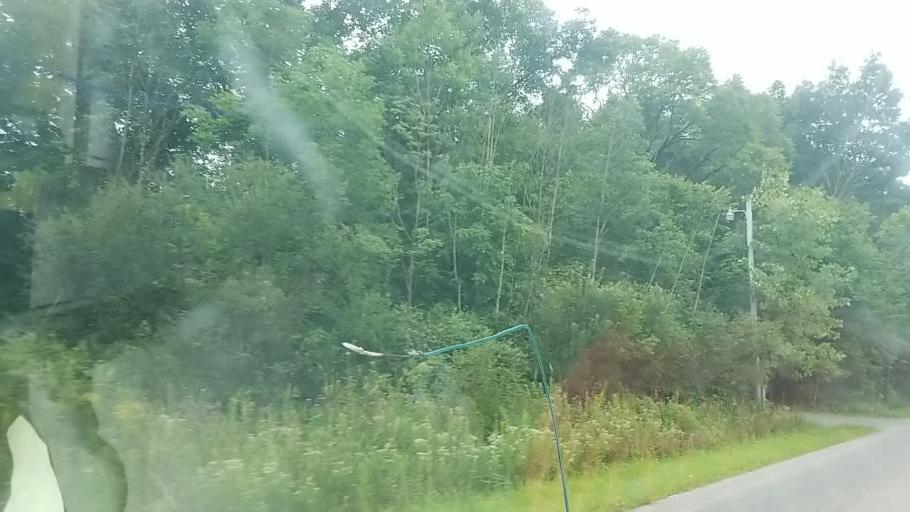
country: US
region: Ohio
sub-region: Delaware County
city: Ashley
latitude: 40.4013
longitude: -82.8527
